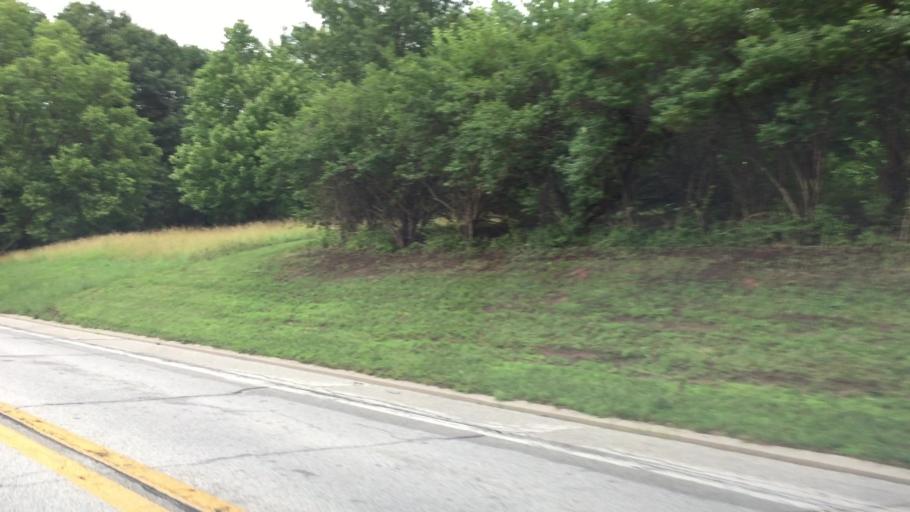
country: US
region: Illinois
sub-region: Hancock County
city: Hamilton
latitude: 40.4022
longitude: -91.3519
